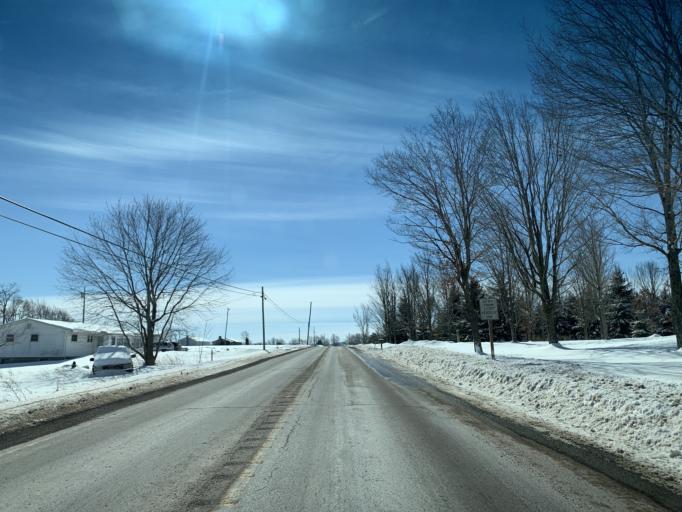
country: US
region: Pennsylvania
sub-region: Somerset County
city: Meyersdale
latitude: 39.7194
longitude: -79.1597
